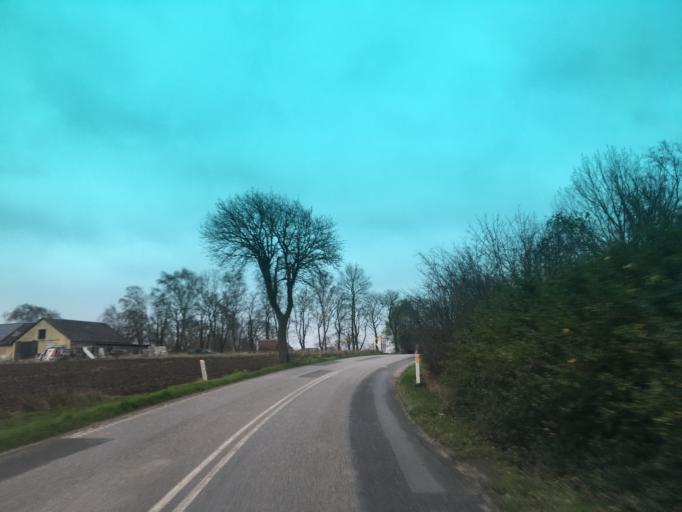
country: DK
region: Zealand
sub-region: Slagelse Kommune
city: Skaelskor
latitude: 55.2477
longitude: 11.4226
